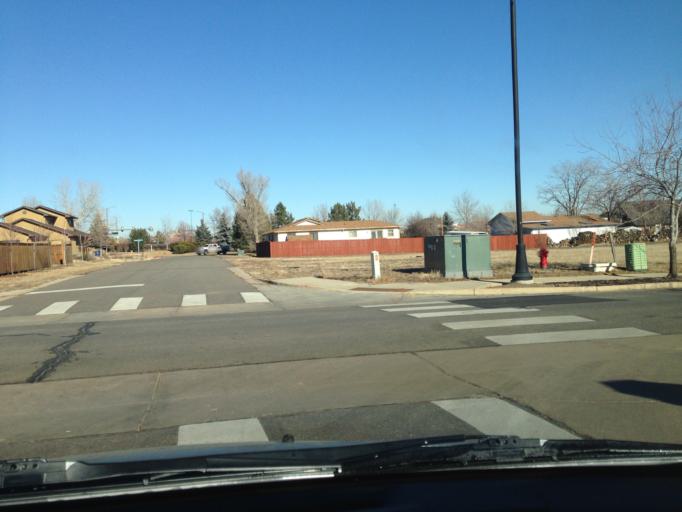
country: US
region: Colorado
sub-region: Boulder County
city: Superior
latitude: 39.9539
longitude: -105.1694
